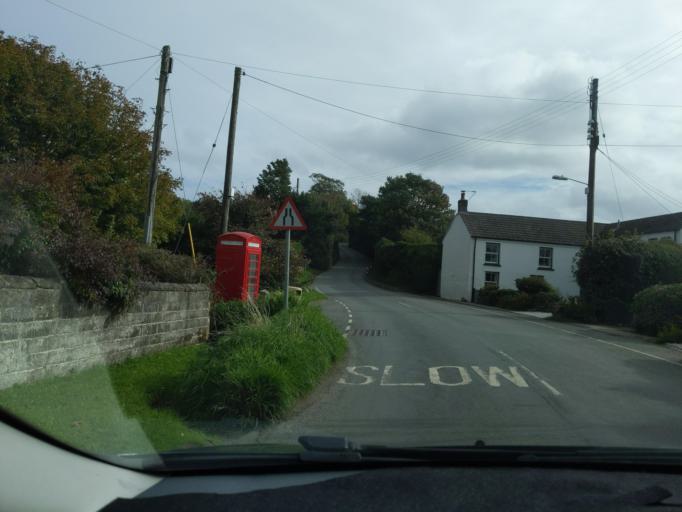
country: GB
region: England
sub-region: Cornwall
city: Mevagissey
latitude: 50.2461
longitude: -4.8075
